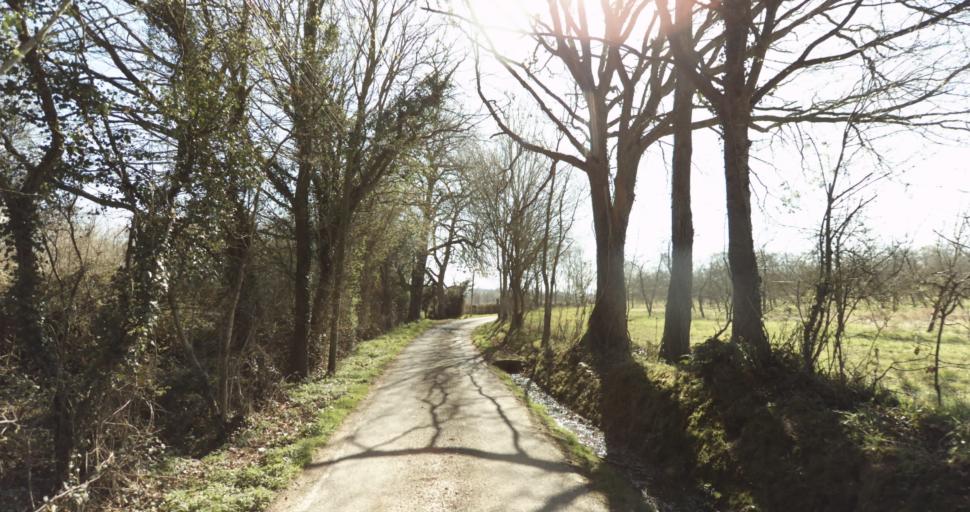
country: FR
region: Lower Normandy
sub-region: Departement du Calvados
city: Livarot
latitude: 49.0060
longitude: 0.0871
